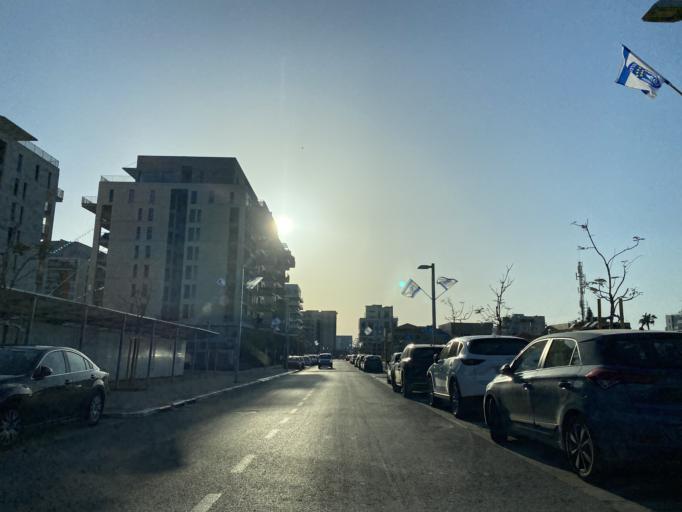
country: IL
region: Tel Aviv
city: Herzliyya
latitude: 32.1617
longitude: 34.8312
